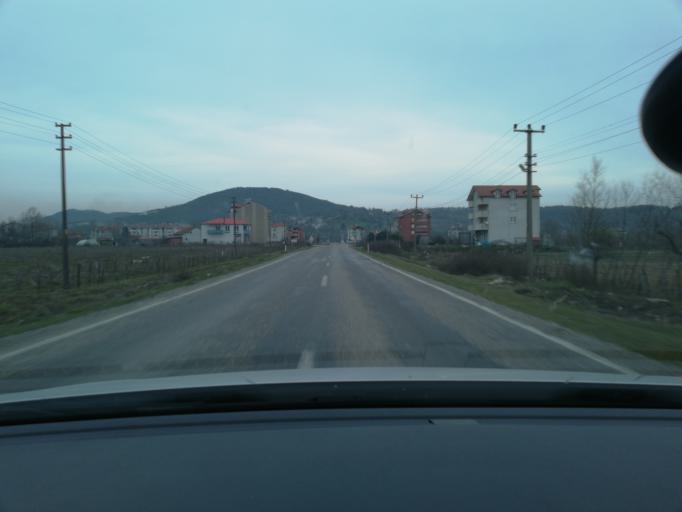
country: TR
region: Zonguldak
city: Saltukova
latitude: 41.5215
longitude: 32.1017
